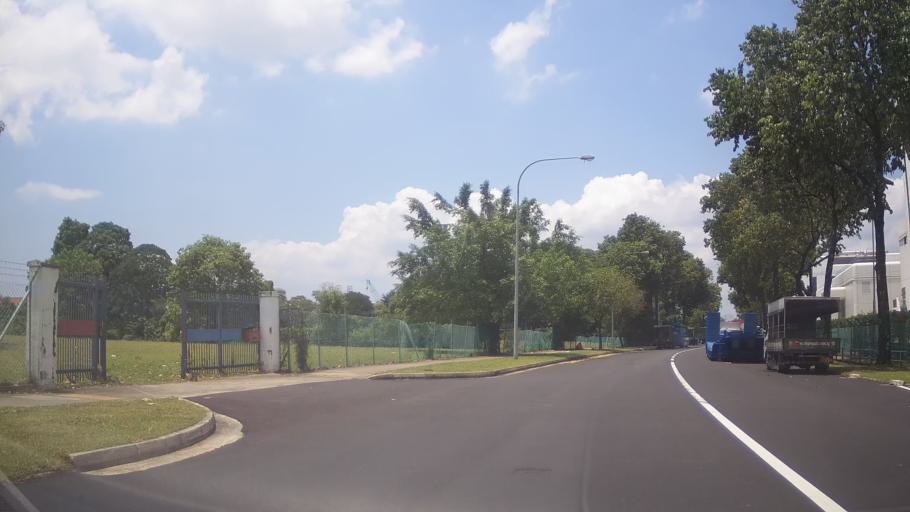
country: MY
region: Johor
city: Johor Bahru
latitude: 1.3067
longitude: 103.6613
